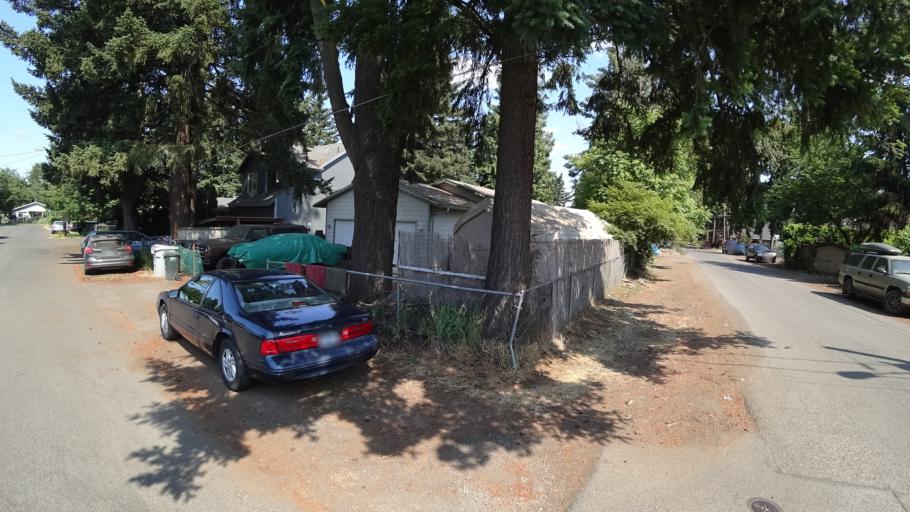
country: US
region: Oregon
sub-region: Multnomah County
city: Lents
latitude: 45.4525
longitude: -122.5812
